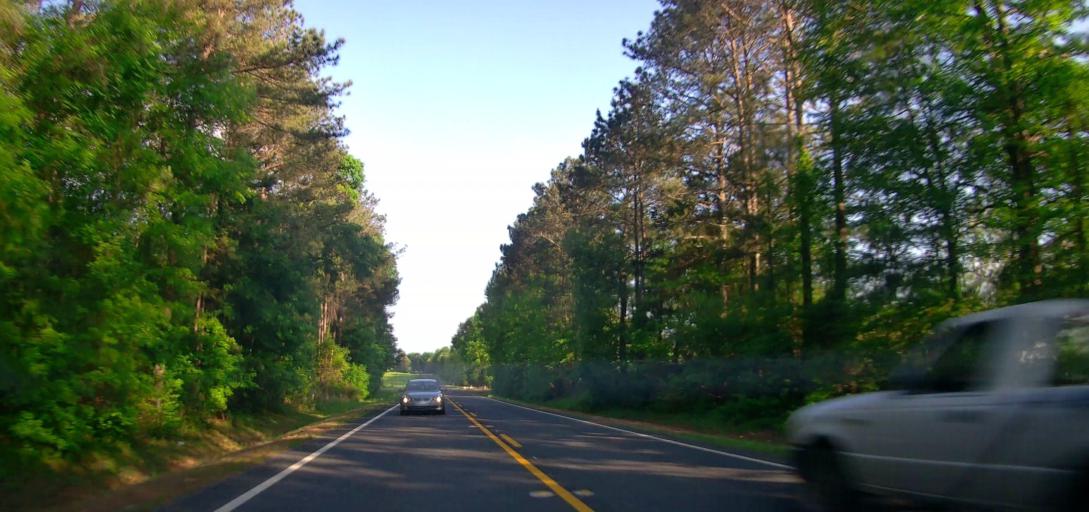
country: US
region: Georgia
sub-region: Jasper County
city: Monticello
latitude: 33.4131
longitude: -83.6066
